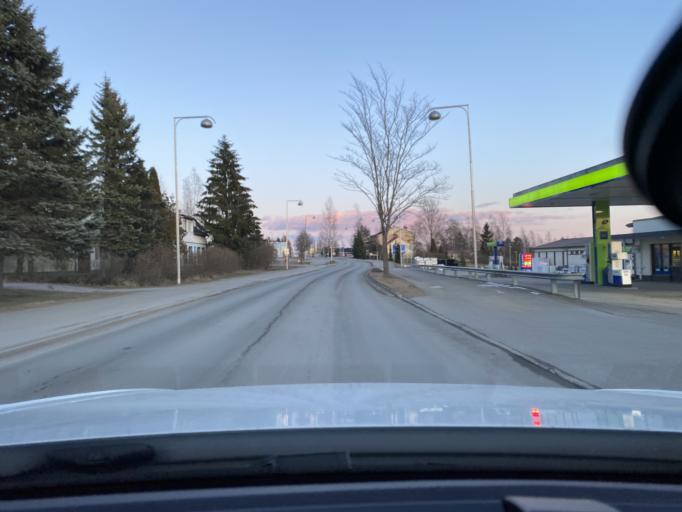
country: FI
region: Pirkanmaa
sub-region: Lounais-Pirkanmaa
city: Punkalaidun
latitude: 61.1128
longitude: 23.1021
